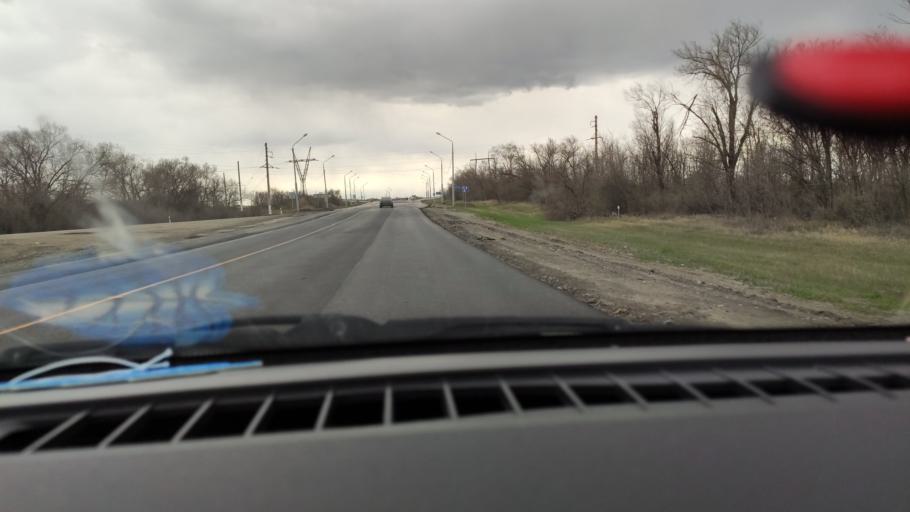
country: RU
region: Saratov
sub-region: Saratovskiy Rayon
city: Saratov
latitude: 51.6717
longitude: 45.9999
